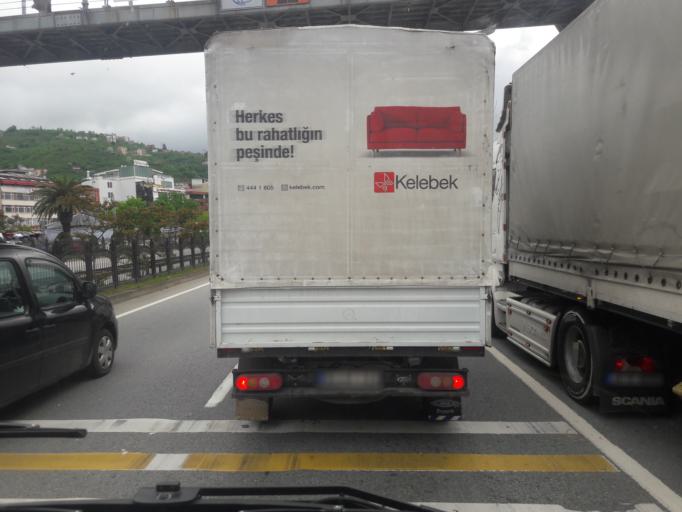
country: TR
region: Giresun
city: Giresun
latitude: 40.9185
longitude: 38.3839
